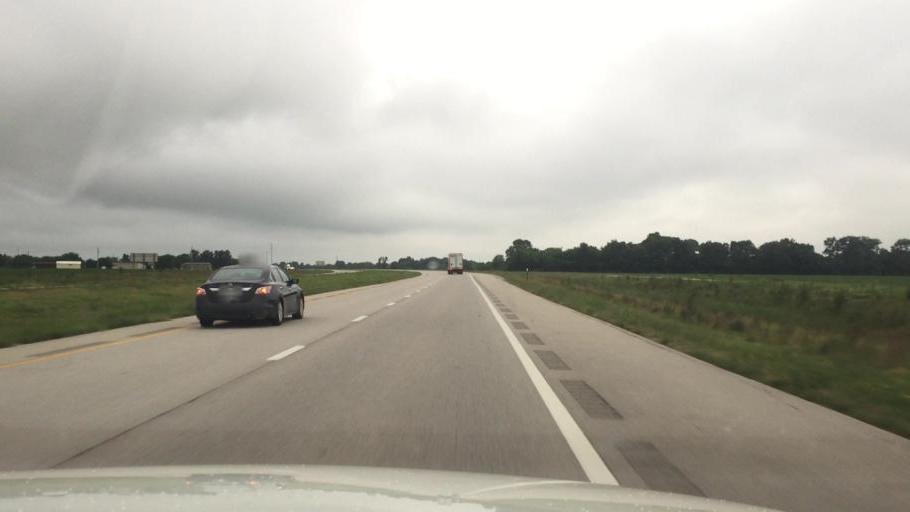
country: US
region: Kansas
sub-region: Montgomery County
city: Coffeyville
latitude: 37.1045
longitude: -95.5883
